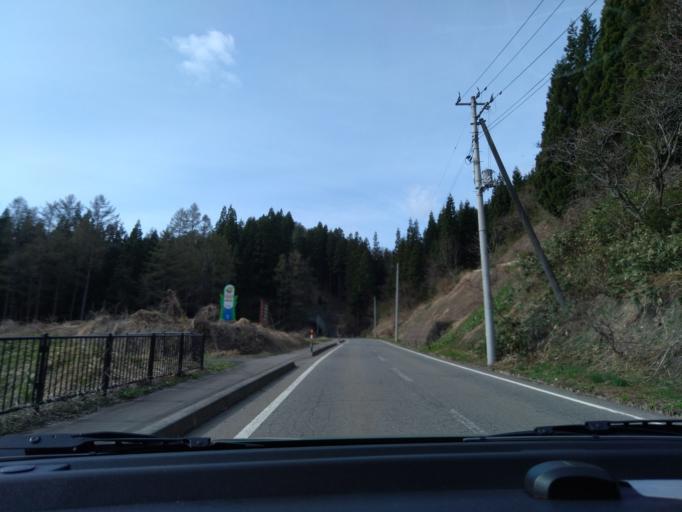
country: JP
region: Akita
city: Yokotemachi
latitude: 39.3102
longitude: 140.5847
